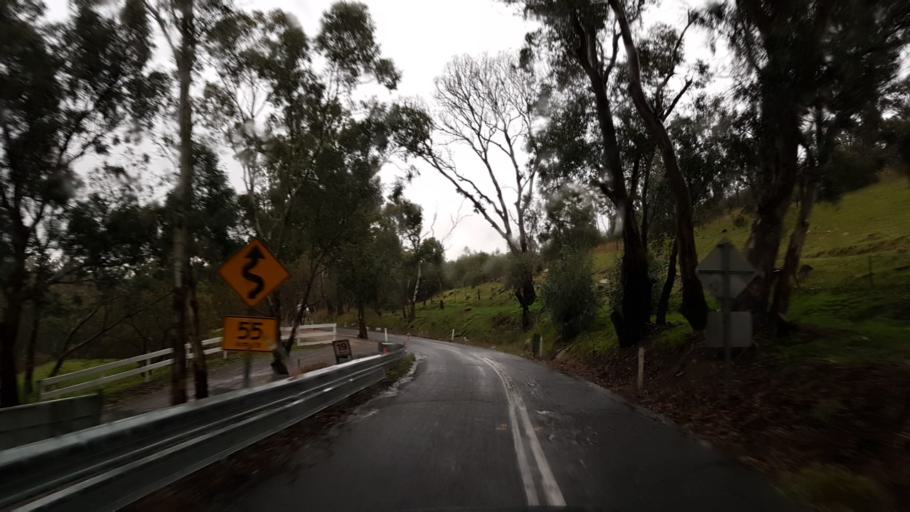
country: AU
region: South Australia
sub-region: Onkaparinga
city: Craigburn Farm
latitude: -35.0643
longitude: 138.6253
